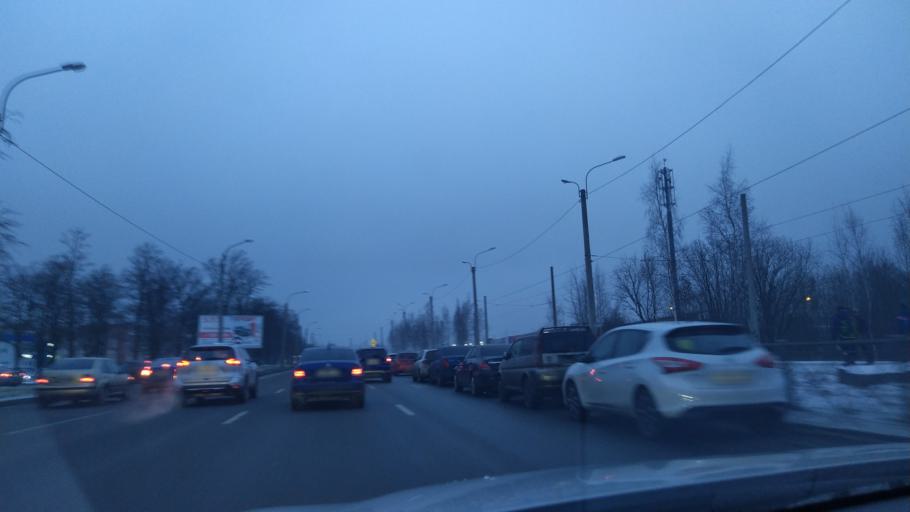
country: RU
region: St.-Petersburg
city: Grazhdanka
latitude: 60.0224
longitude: 30.4324
